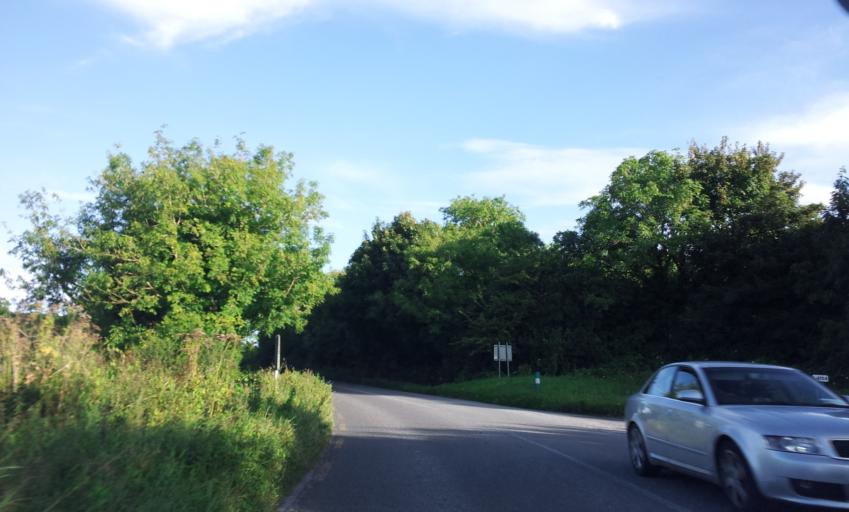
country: IE
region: Munster
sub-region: An Clar
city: Ennis
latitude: 52.9035
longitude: -9.0411
